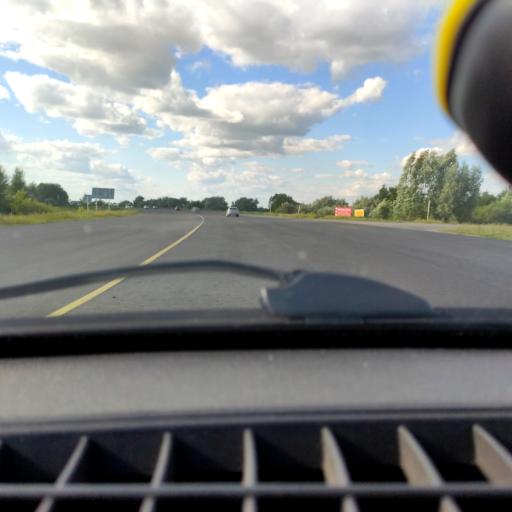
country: RU
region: Samara
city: Tol'yatti
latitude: 53.6598
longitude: 49.4251
